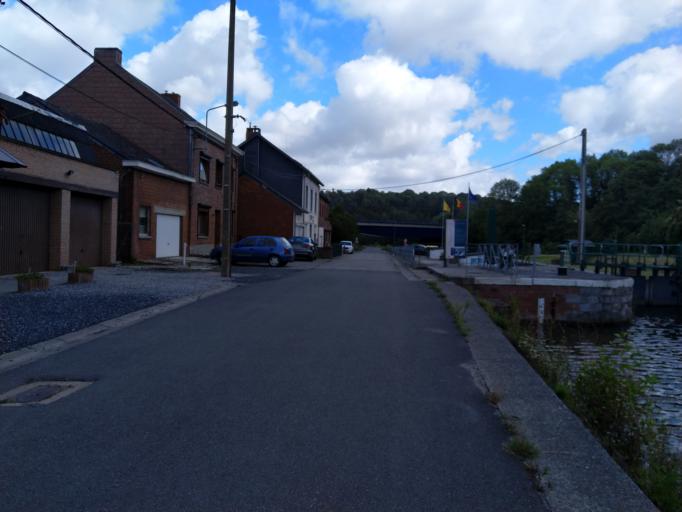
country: BE
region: Wallonia
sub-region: Province du Hainaut
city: Lobbes
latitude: 50.3437
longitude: 4.2723
